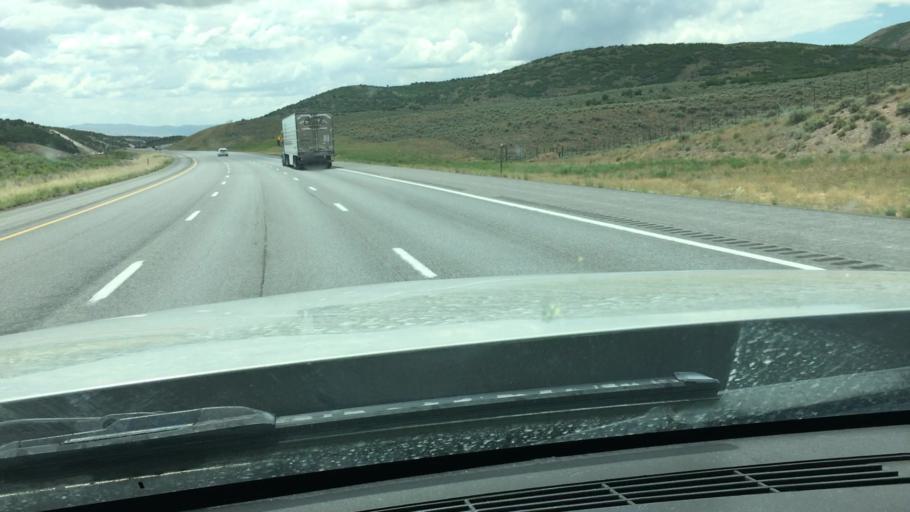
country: US
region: Utah
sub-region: Beaver County
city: Beaver
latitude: 38.4654
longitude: -112.6194
